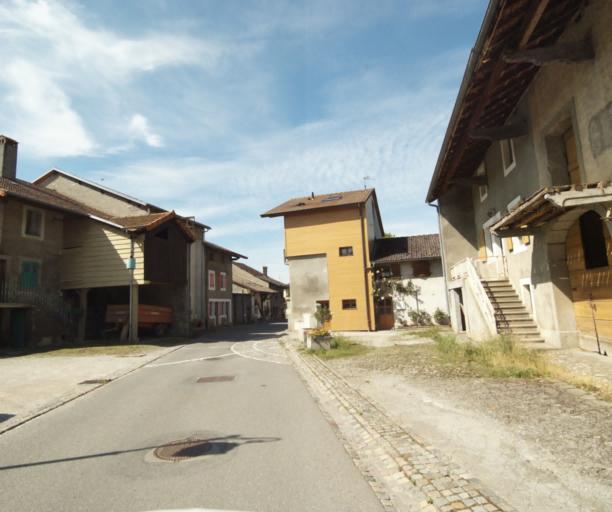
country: FR
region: Rhone-Alpes
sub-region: Departement de la Haute-Savoie
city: Anthy-sur-Leman
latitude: 46.3479
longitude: 6.4109
